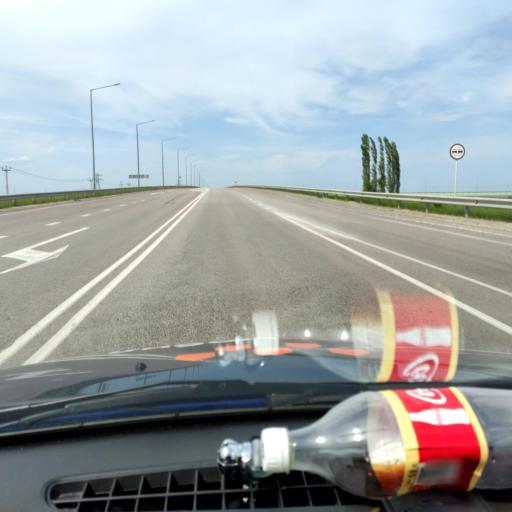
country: RU
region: Voronezj
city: Novaya Usman'
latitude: 51.5869
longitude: 39.3744
